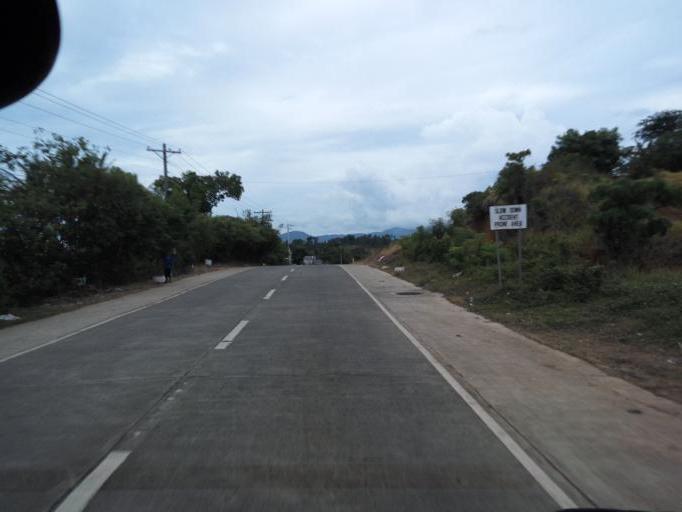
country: PH
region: Cagayan Valley
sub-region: Province of Cagayan
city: Tapel
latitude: 18.2873
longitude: 122.0220
